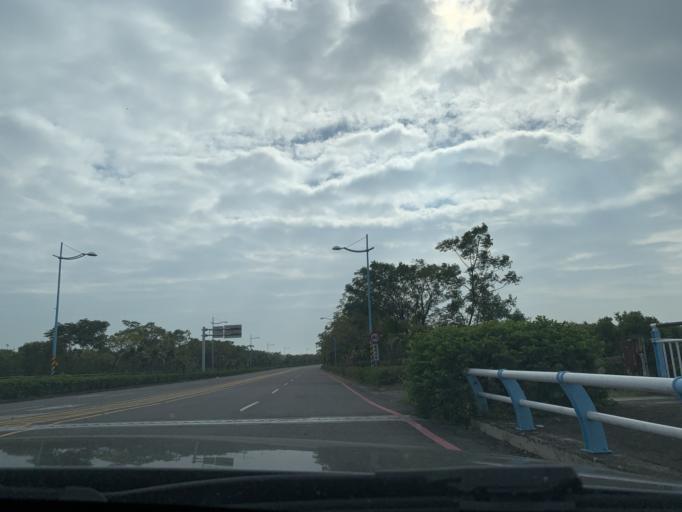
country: TW
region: Taiwan
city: Fengshan
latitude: 22.4411
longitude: 120.4930
